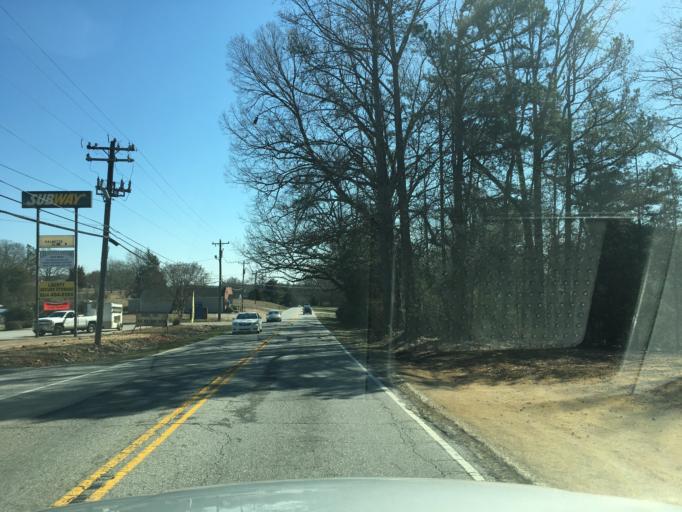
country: US
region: South Carolina
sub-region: Pickens County
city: Liberty
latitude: 34.7820
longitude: -82.6797
